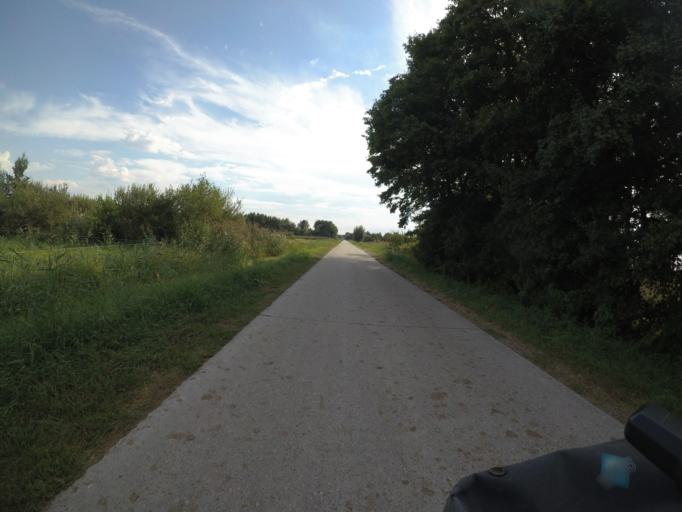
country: NL
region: Overijssel
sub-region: Gemeente Steenwijkerland
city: Wanneperveen
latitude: 52.6508
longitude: 6.1201
